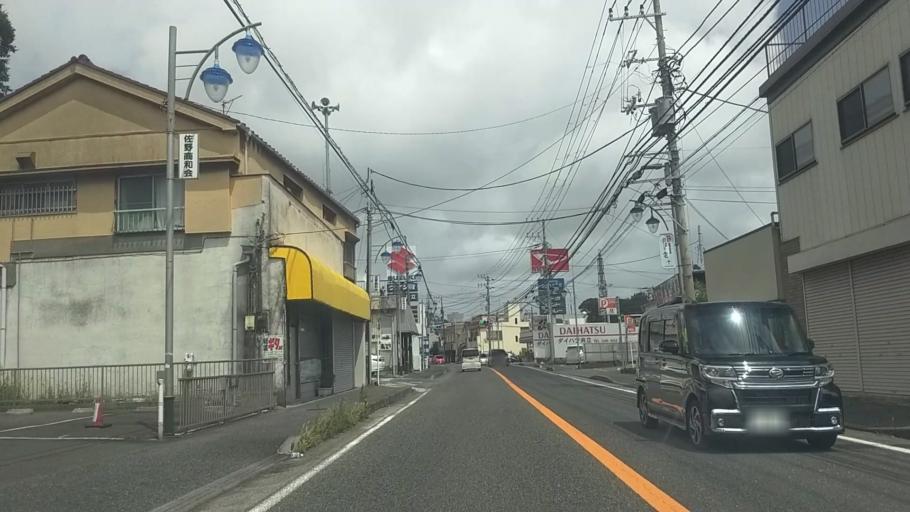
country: JP
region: Kanagawa
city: Yokosuka
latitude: 35.2622
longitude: 139.6689
